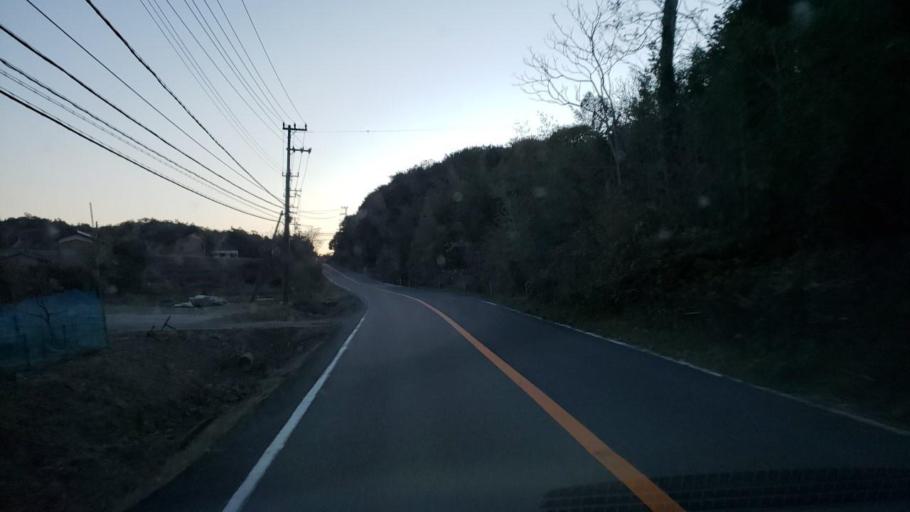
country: JP
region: Hyogo
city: Fukura
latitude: 34.2850
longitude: 134.6841
